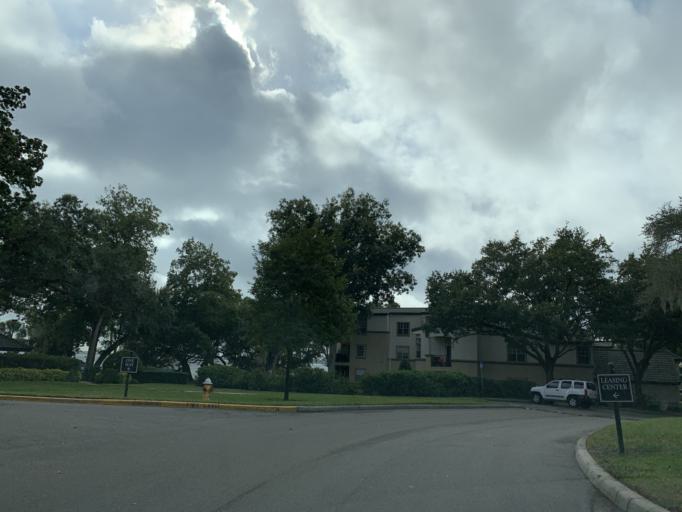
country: US
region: Florida
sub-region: Pinellas County
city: South Highpoint
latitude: 27.9547
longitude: -82.7231
